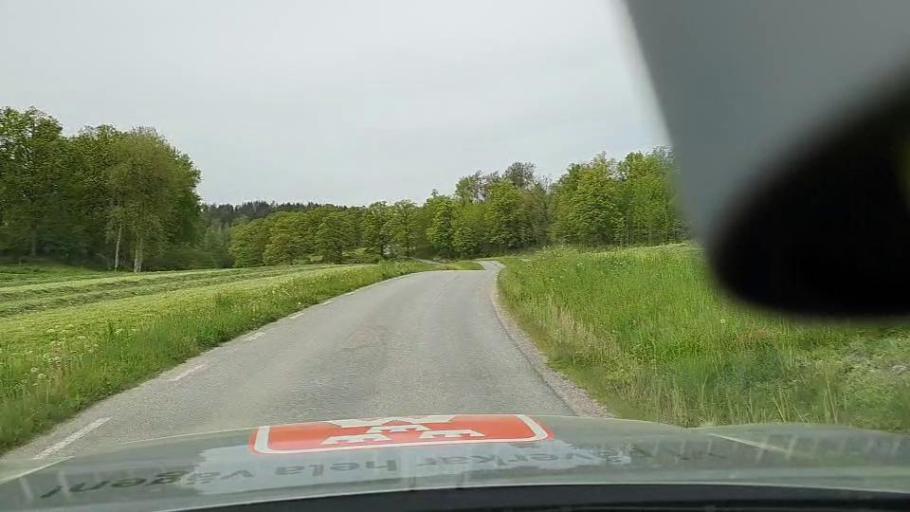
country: SE
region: Soedermanland
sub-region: Flens Kommun
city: Halleforsnas
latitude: 59.1020
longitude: 16.4772
